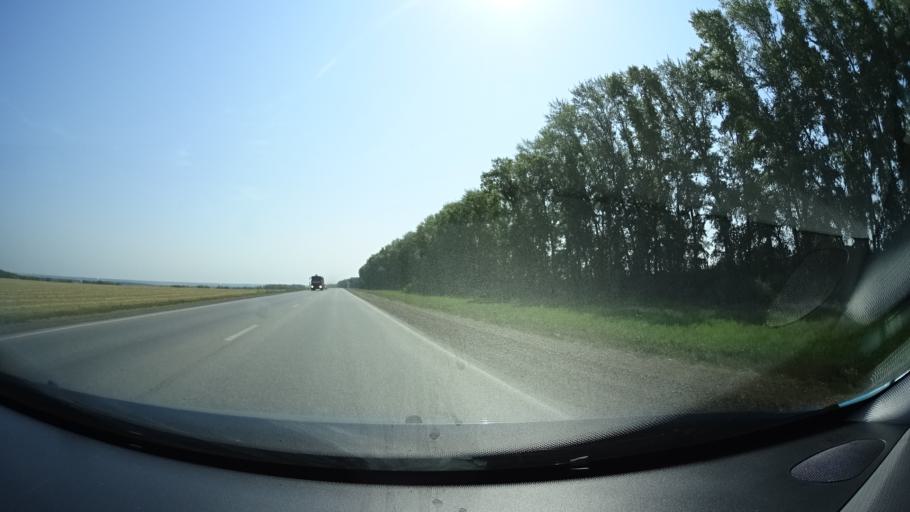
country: RU
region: Bashkortostan
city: Kabakovo
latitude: 54.4726
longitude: 55.9413
